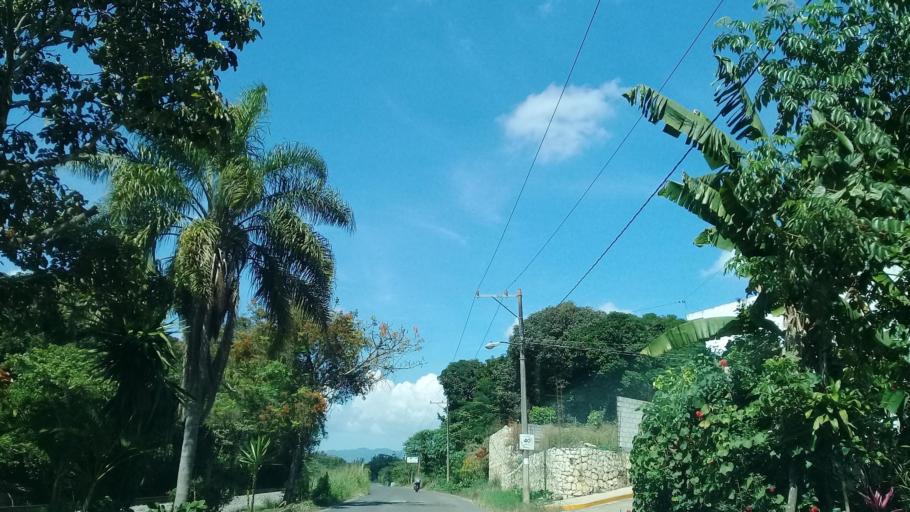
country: MX
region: Veracruz
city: Amatlan de los Reyes
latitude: 18.8392
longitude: -96.9211
